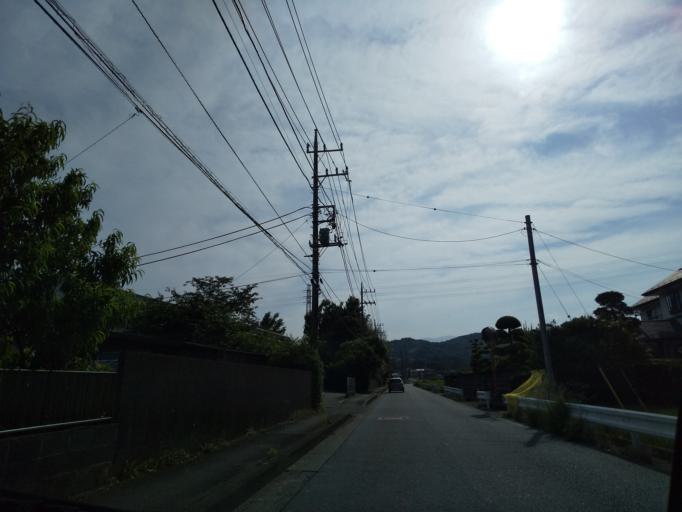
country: JP
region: Kanagawa
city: Zama
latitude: 35.4992
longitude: 139.3501
